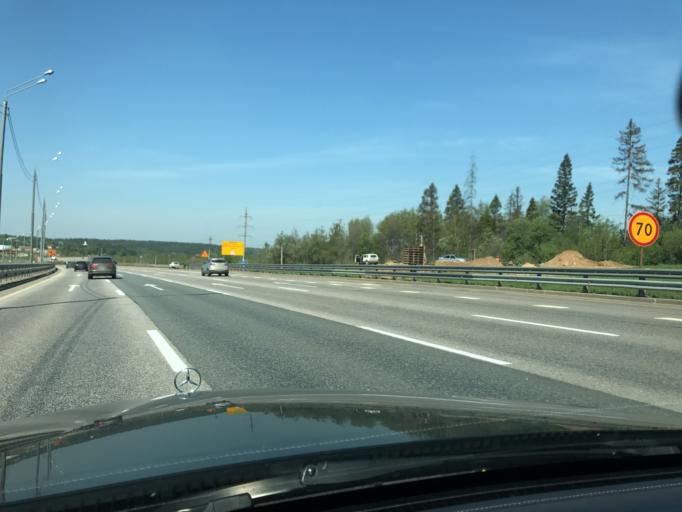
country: RU
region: Moskovskaya
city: Pavlovskaya Sloboda
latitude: 55.7875
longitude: 37.1313
